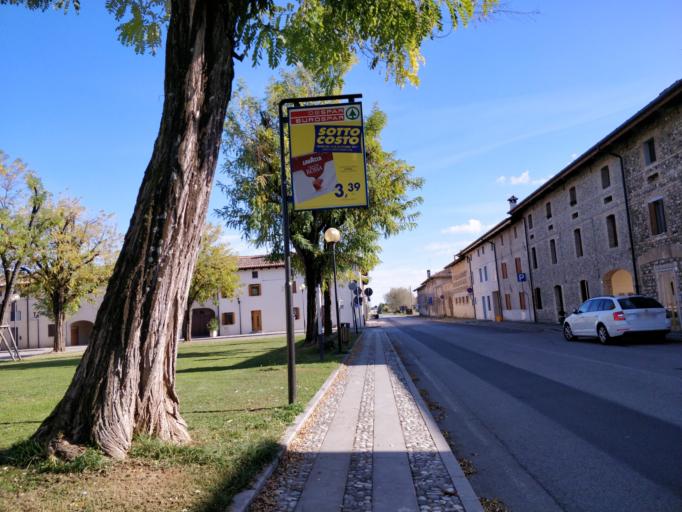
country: IT
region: Friuli Venezia Giulia
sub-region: Provincia di Udine
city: Codroipo
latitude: 45.9478
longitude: 13.0130
